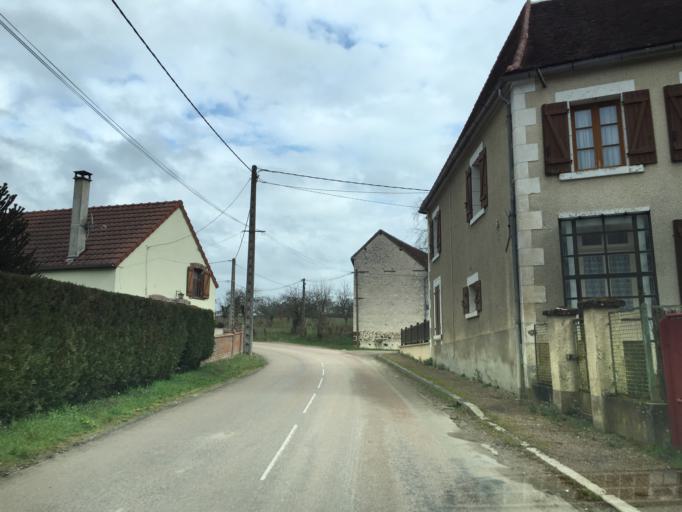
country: FR
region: Bourgogne
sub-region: Departement de l'Yonne
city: Pourrain
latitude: 47.7909
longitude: 3.3979
